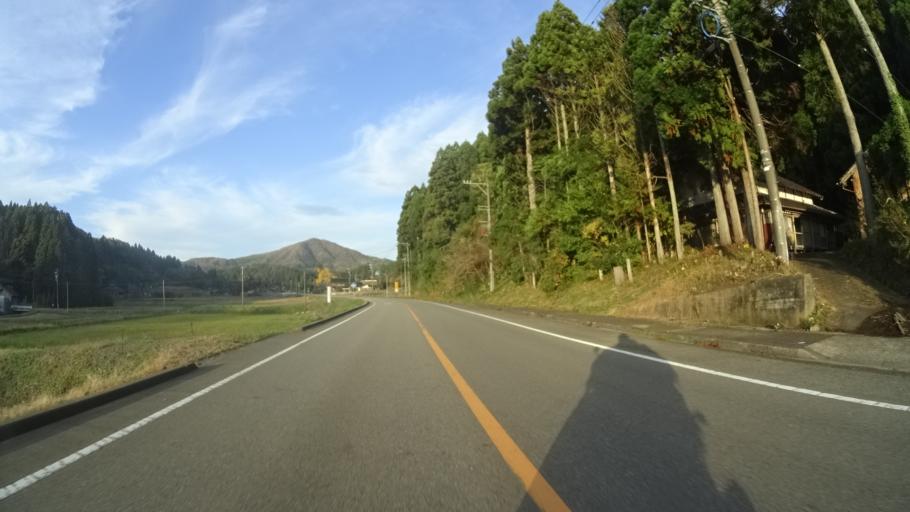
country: JP
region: Ishikawa
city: Nanao
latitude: 37.1871
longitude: 136.7154
